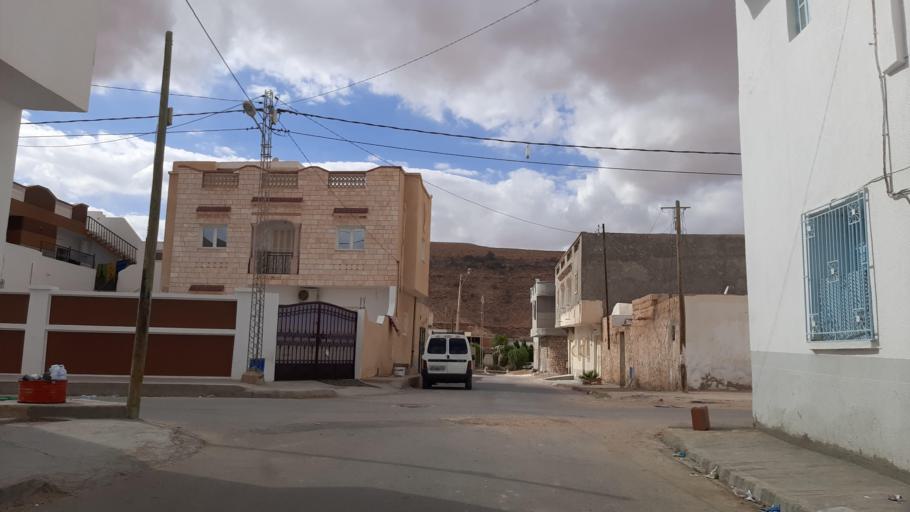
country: TN
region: Tataouine
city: Tataouine
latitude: 32.9352
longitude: 10.4505
